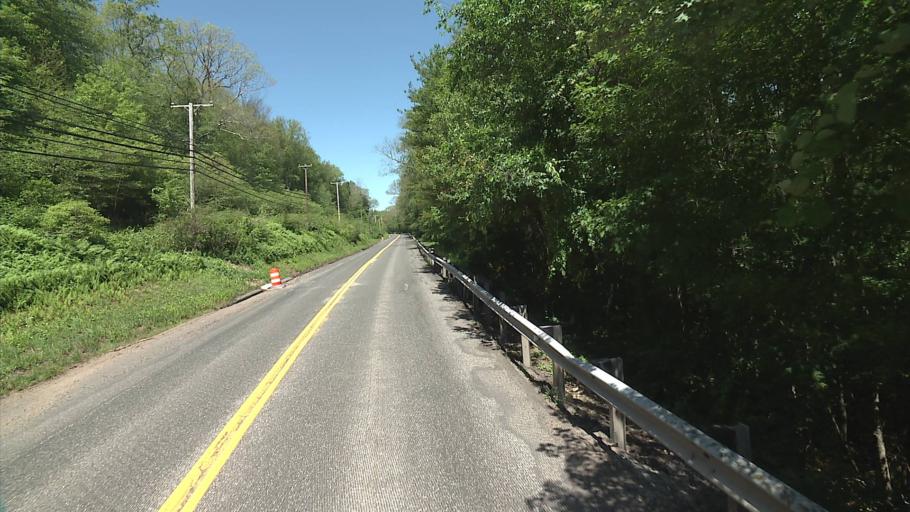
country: US
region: Connecticut
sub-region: Middlesex County
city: East Hampton
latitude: 41.5621
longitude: -72.4610
